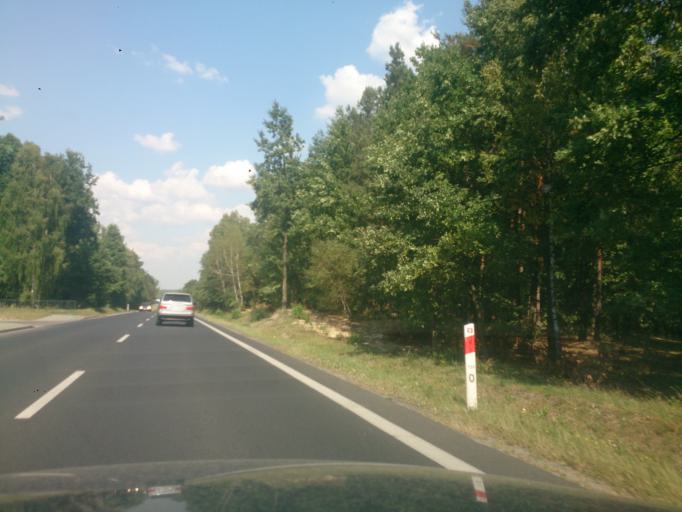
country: PL
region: Subcarpathian Voivodeship
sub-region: Powiat kolbuszowski
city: Cmolas
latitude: 50.2986
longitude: 21.7438
